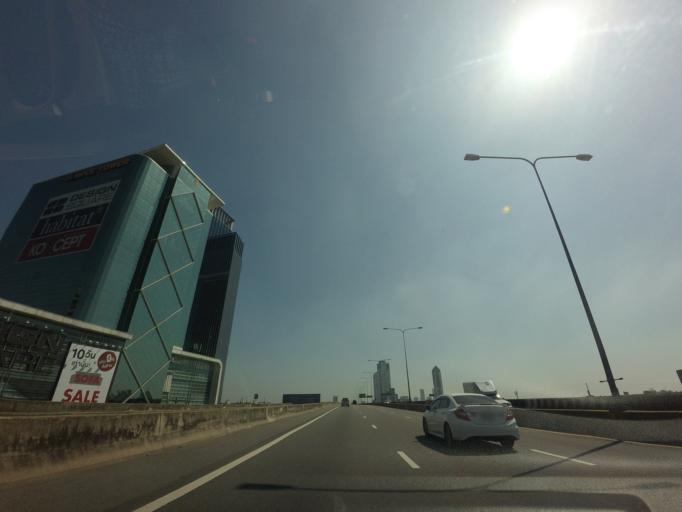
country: TH
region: Bangkok
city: Bang Na
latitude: 13.6663
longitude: 100.6422
